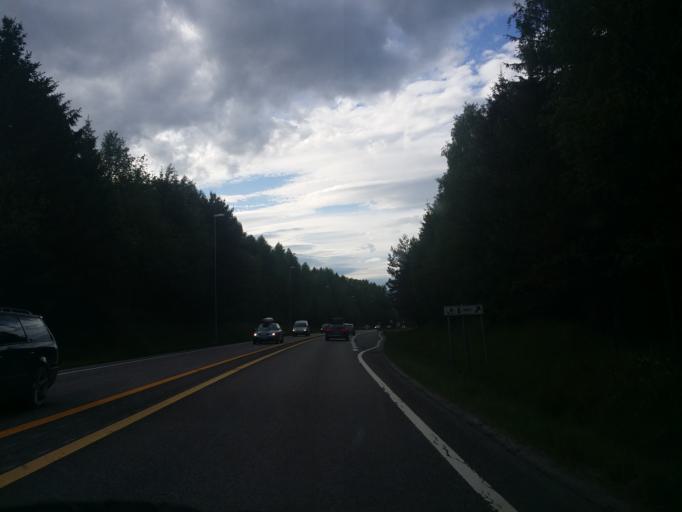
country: NO
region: Hedmark
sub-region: Ringsaker
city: Brumunddal
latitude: 60.8654
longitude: 10.9519
